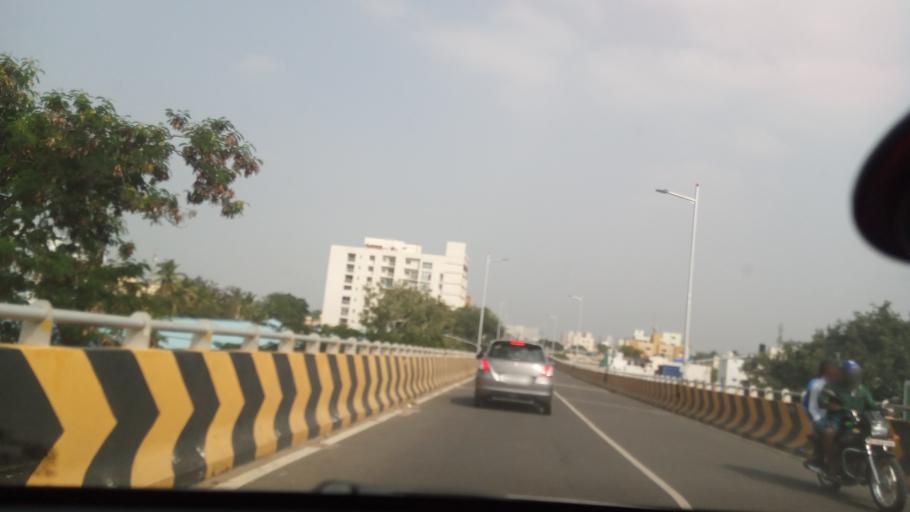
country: IN
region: Tamil Nadu
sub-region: Coimbatore
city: Coimbatore
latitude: 11.0211
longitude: 76.9752
